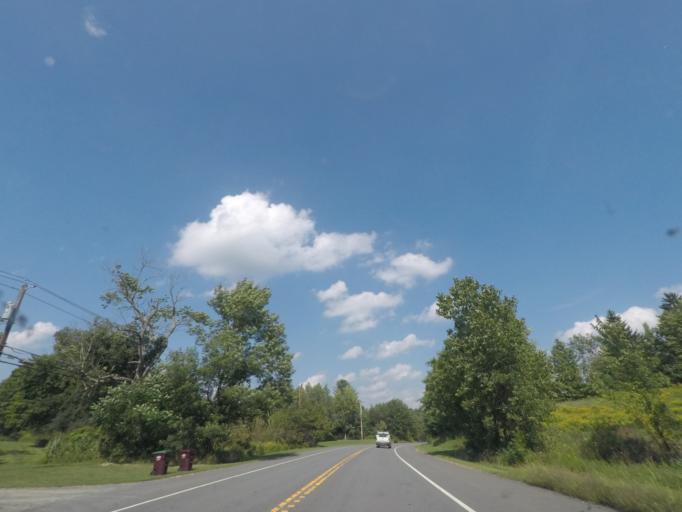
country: US
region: New York
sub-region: Rensselaer County
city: Hoosick Falls
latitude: 42.8425
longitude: -73.4791
